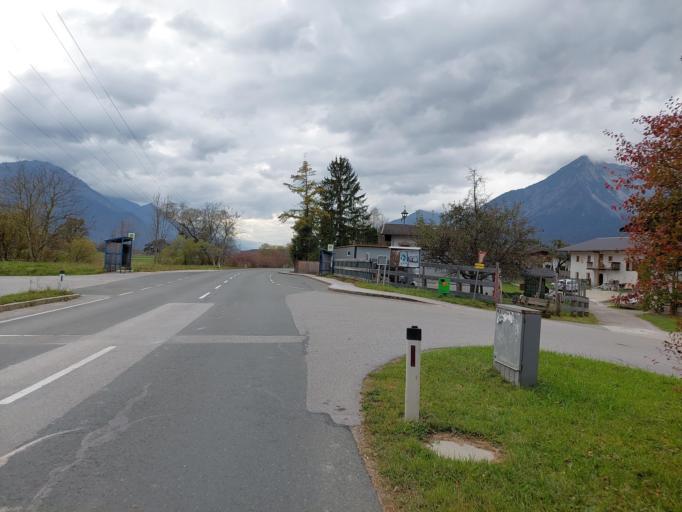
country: AT
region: Tyrol
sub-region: Politischer Bezirk Kufstein
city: Munster
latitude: 47.4281
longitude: 11.8552
